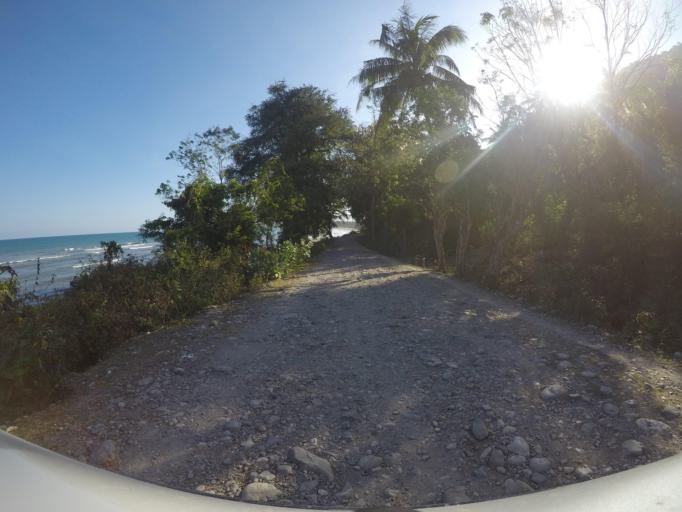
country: TL
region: Viqueque
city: Viqueque
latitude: -8.7991
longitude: 126.5921
